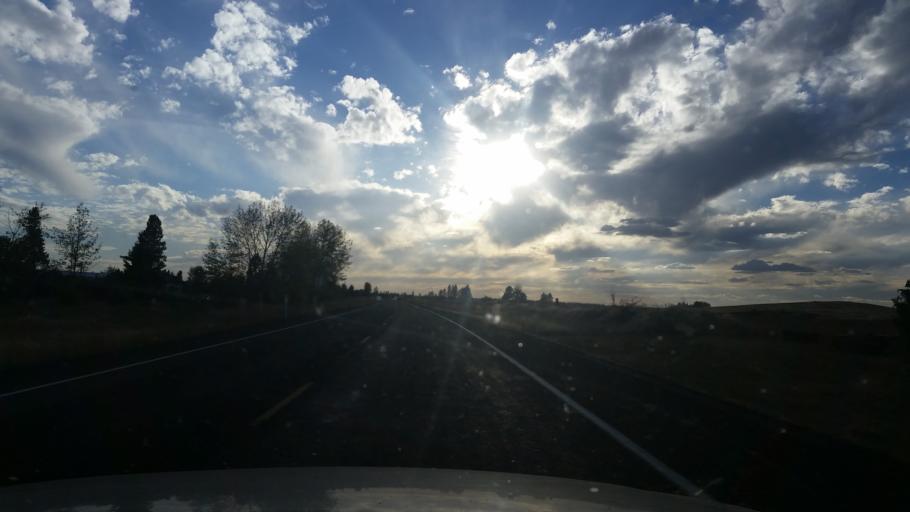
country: US
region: Washington
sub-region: Spokane County
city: Cheney
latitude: 47.4690
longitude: -117.6293
